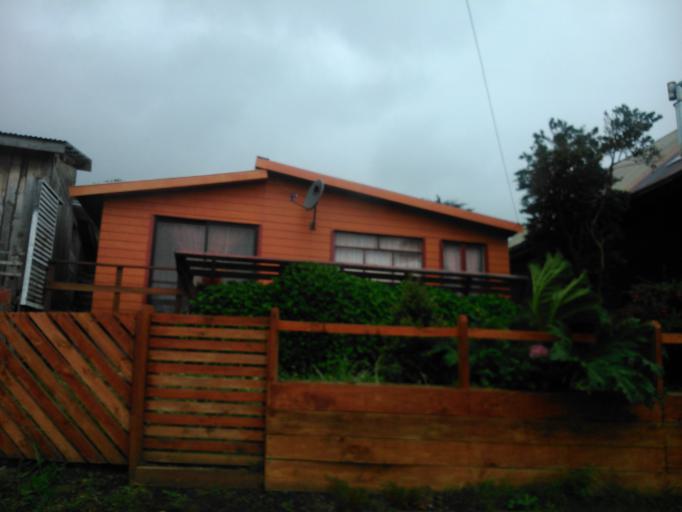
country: CL
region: Araucania
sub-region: Provincia de Cautin
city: Carahue
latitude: -38.8100
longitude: -73.3986
